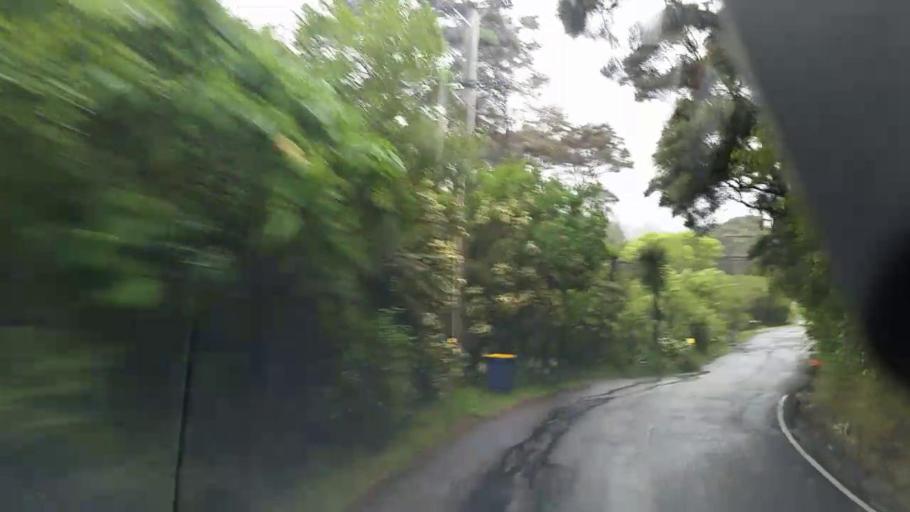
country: NZ
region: Auckland
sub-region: Auckland
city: Waitakere
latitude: -36.9035
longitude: 174.5739
